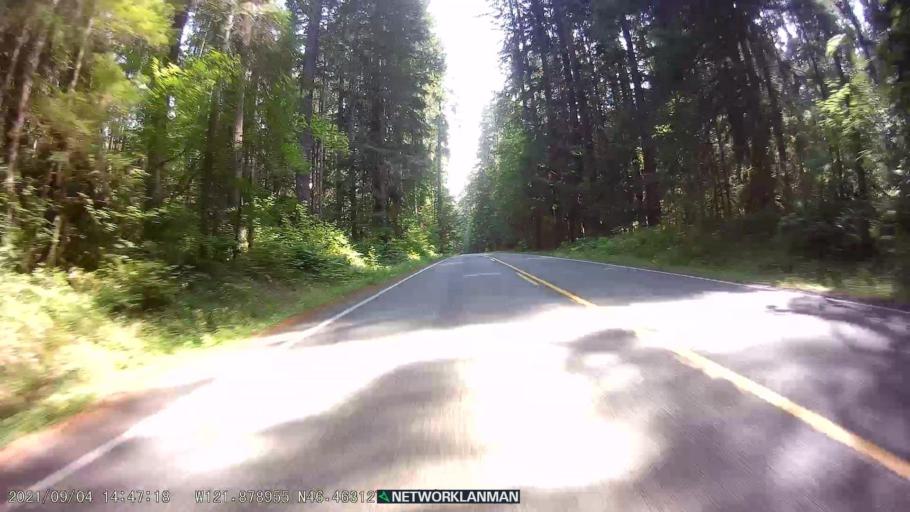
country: US
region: Washington
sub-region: Lewis County
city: Morton
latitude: 46.4634
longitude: -121.8792
